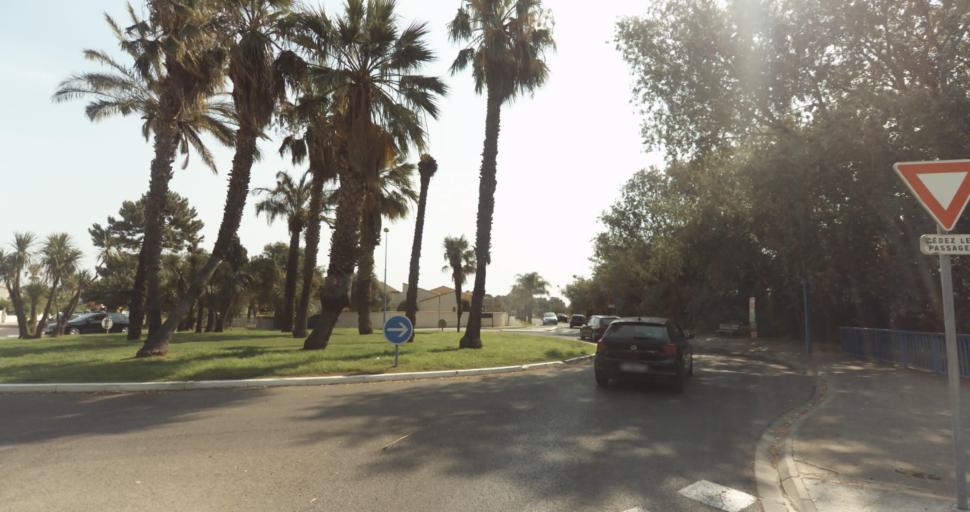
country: FR
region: Languedoc-Roussillon
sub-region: Departement des Pyrenees-Orientales
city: Saint-Cyprien-Plage
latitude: 42.6177
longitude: 3.0296
